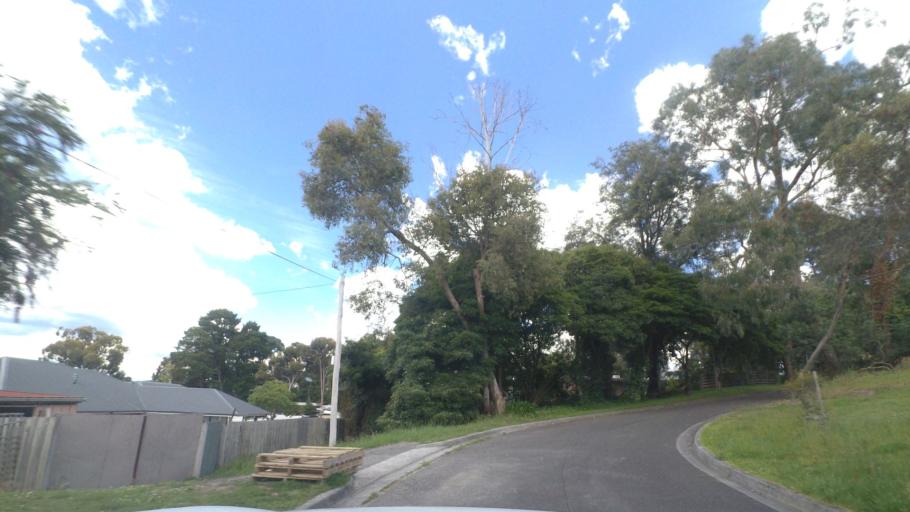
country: AU
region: Victoria
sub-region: Maroondah
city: Croydon South
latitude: -37.8109
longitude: 145.2639
